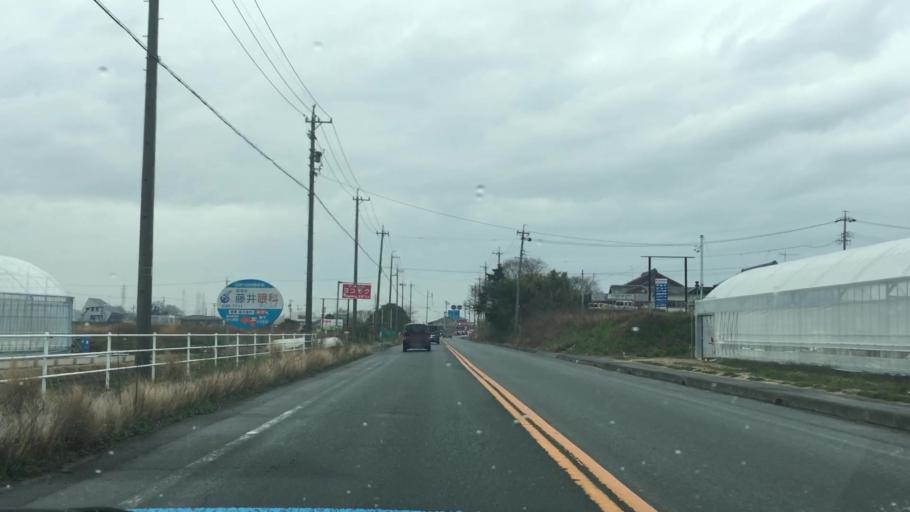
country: JP
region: Aichi
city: Toyohashi
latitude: 34.7148
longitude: 137.3908
